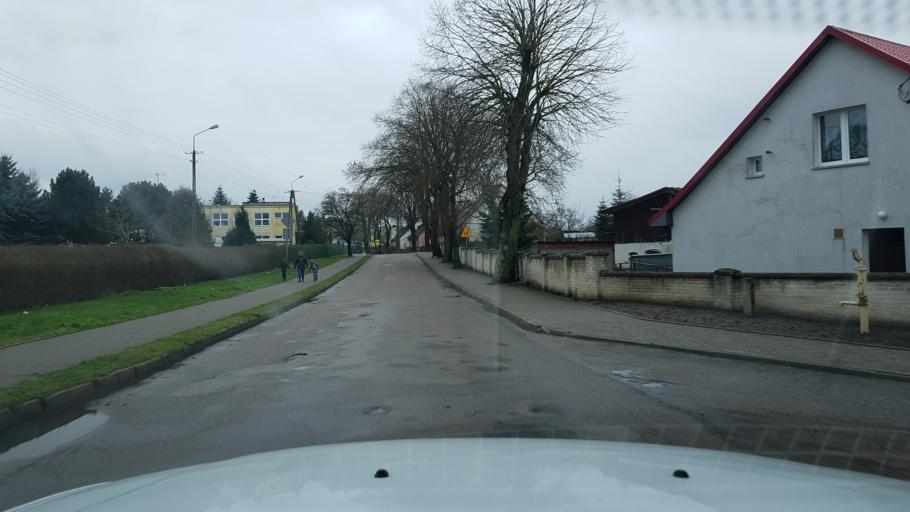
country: PL
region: West Pomeranian Voivodeship
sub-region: Powiat kolobrzeski
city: Grzybowo
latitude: 54.0956
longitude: 15.4352
